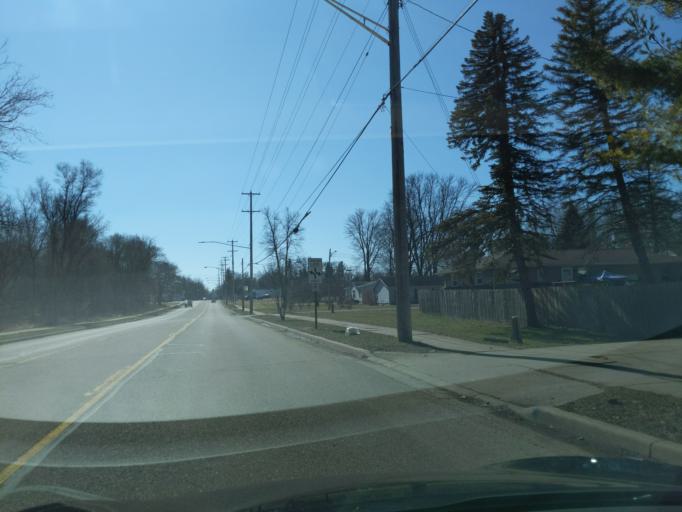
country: US
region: Michigan
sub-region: Ingham County
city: Holt
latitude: 42.6722
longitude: -84.5629
